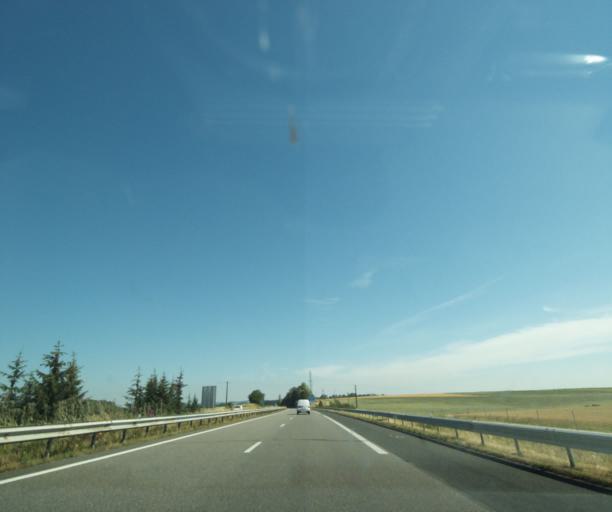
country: FR
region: Lorraine
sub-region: Departement des Vosges
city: Bulgneville
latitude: 48.2522
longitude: 5.8647
